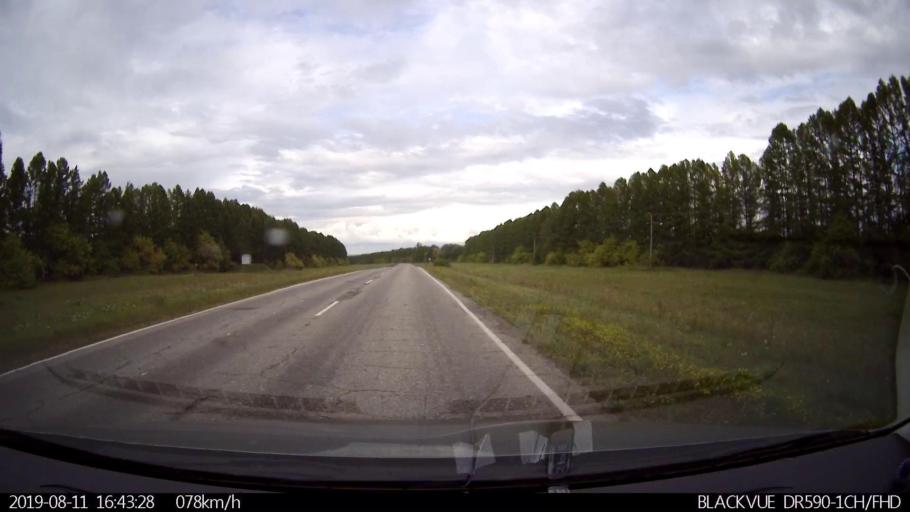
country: RU
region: Ulyanovsk
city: Mayna
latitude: 54.1694
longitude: 47.6725
